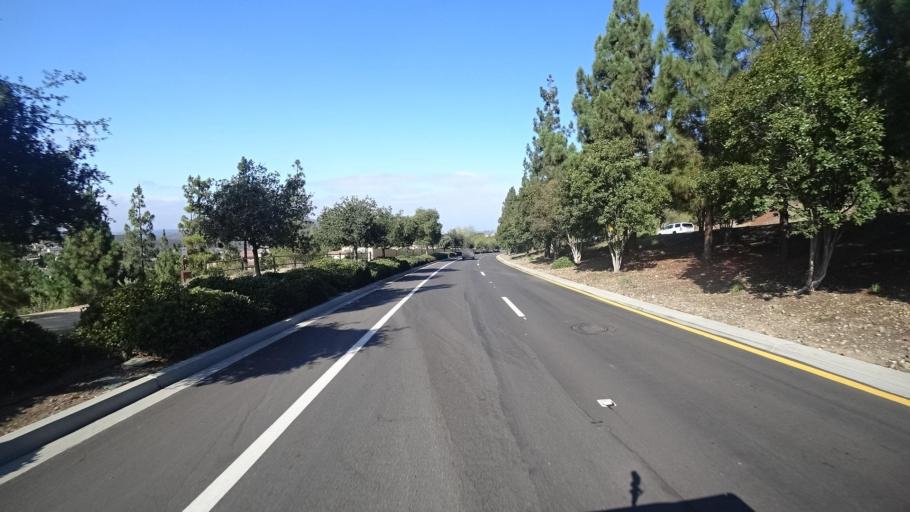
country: US
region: California
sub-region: San Diego County
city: Lake San Marcos
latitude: 33.1019
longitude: -117.1895
